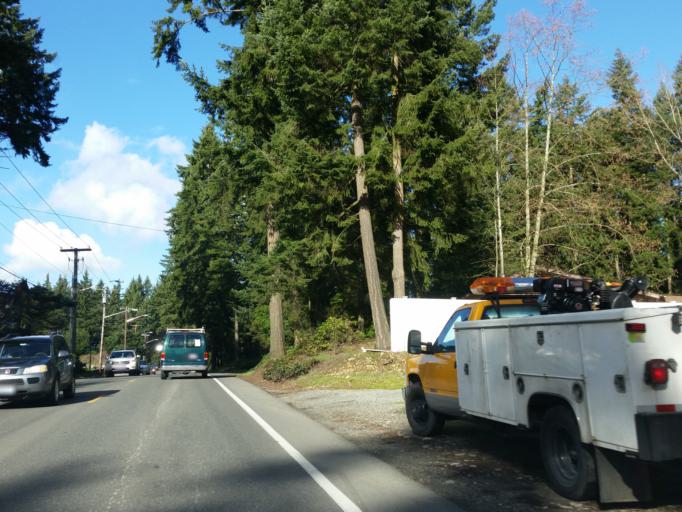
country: US
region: Washington
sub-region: Pierce County
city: South Hill
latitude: 47.1385
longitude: -122.2642
